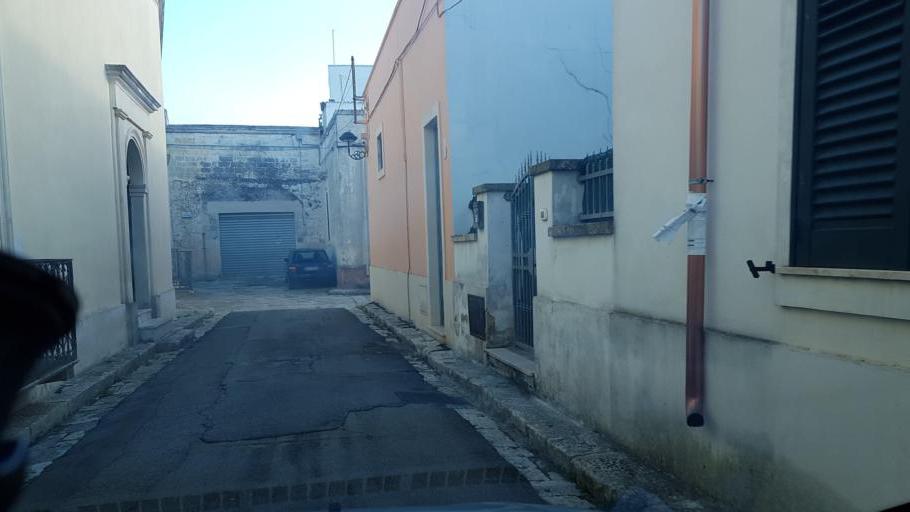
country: IT
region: Apulia
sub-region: Provincia di Lecce
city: Guagnano
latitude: 40.4029
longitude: 17.9513
